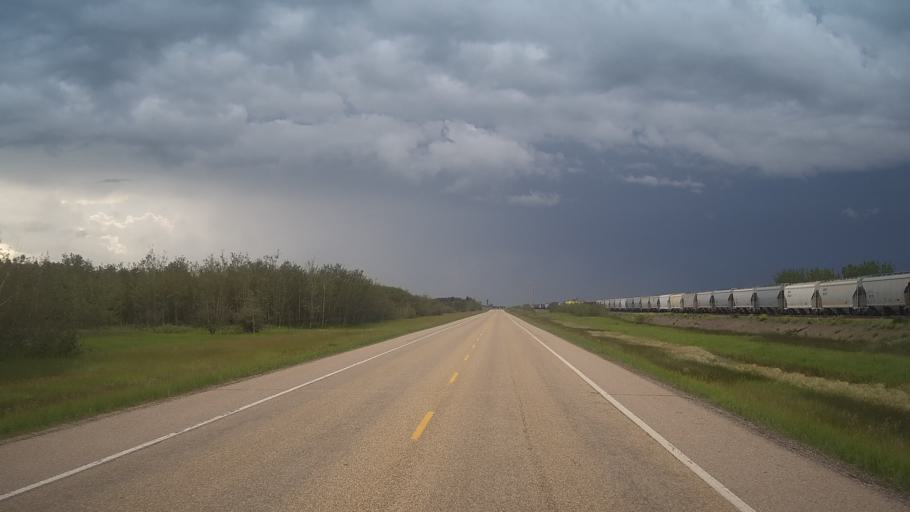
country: CA
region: Alberta
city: Tofield
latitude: 53.2768
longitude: -112.3934
